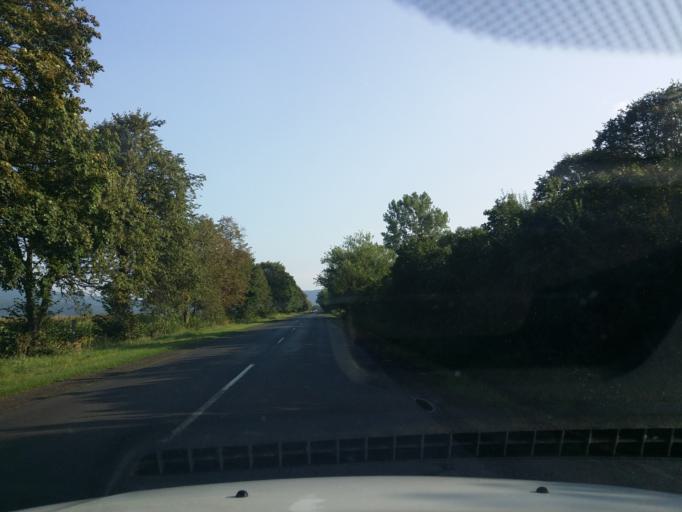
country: HU
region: Borsod-Abauj-Zemplen
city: Abaujszanto
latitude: 48.3166
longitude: 21.2003
